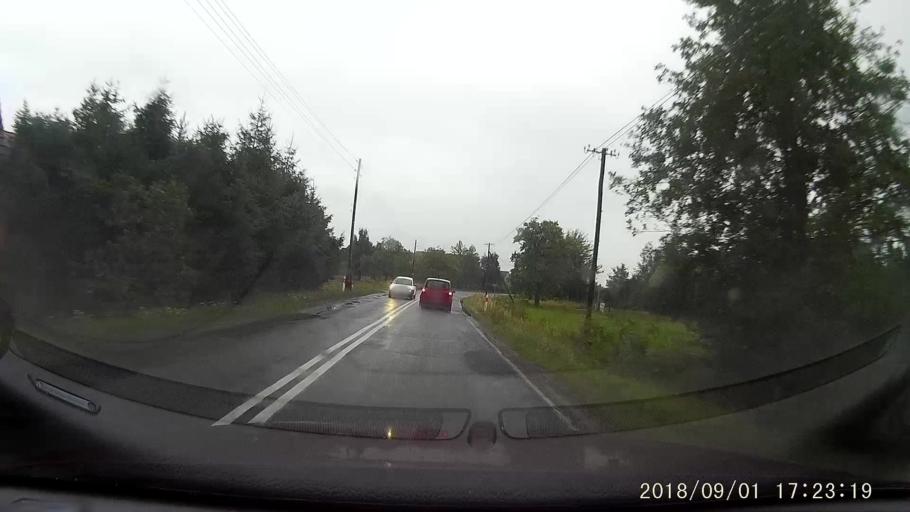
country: PL
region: Lubusz
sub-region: Powiat zaganski
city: Zagan
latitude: 51.7004
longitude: 15.2967
